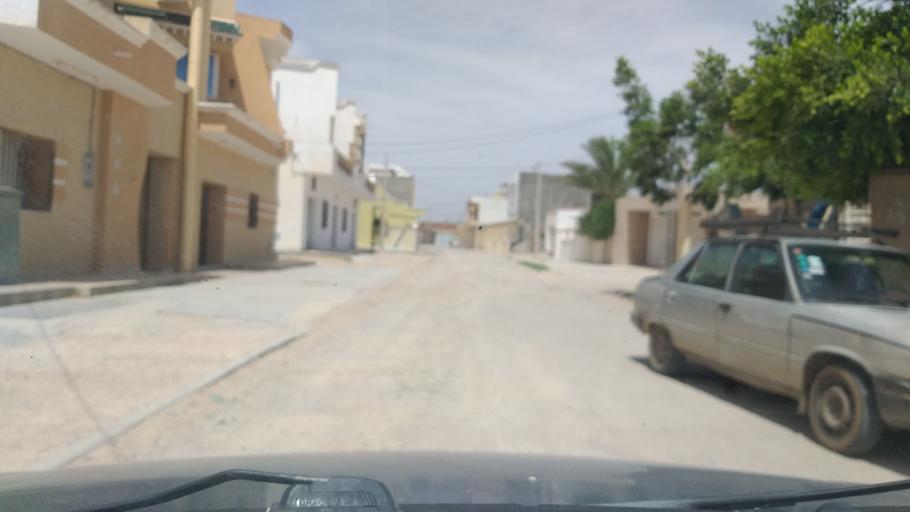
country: TN
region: Al Mahdiyah
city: El Jem
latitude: 35.2951
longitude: 10.6965
